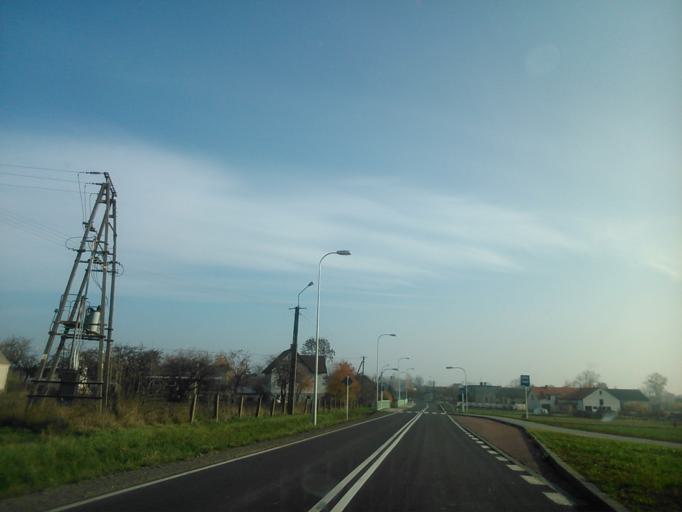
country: PL
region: Warmian-Masurian Voivodeship
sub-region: Powiat dzialdowski
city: Lidzbark
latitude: 53.2376
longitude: 19.9353
